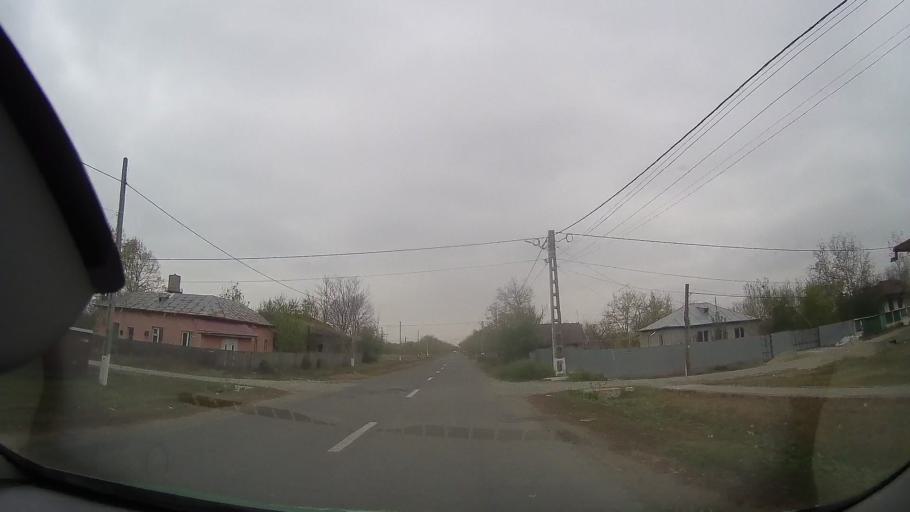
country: RO
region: Ialomita
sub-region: Comuna Valea Macrisului
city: Valea Macrisului
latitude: 44.7443
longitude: 26.8295
